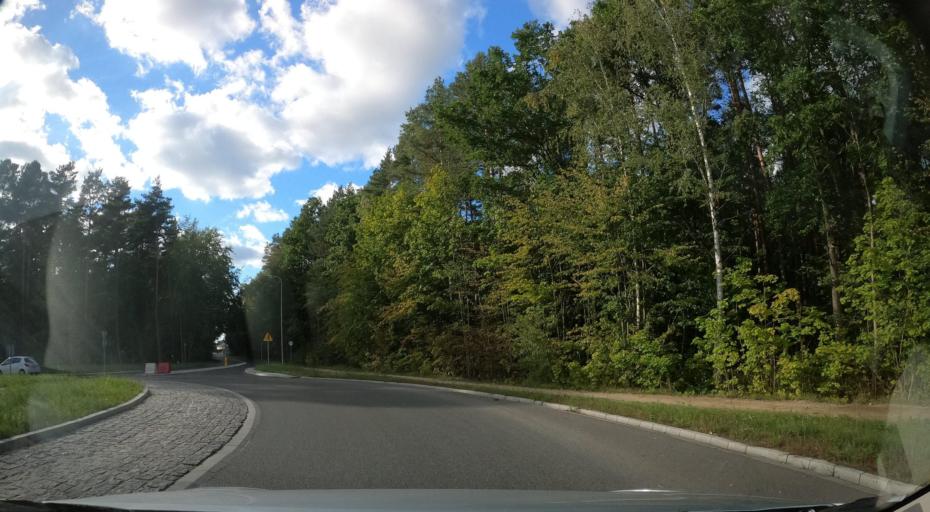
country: PL
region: Pomeranian Voivodeship
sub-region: Powiat wejherowski
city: Luzino
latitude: 54.5689
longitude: 18.0508
